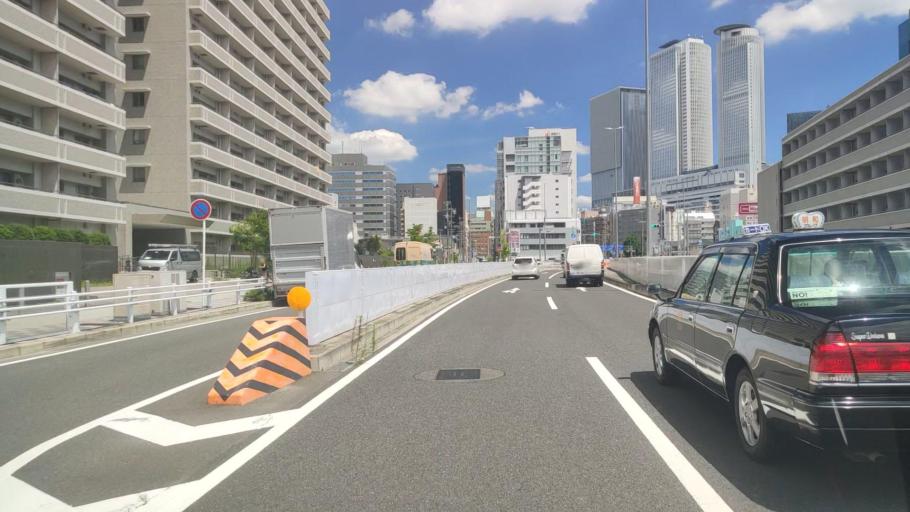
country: JP
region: Aichi
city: Nagoya-shi
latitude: 35.1645
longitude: 136.8803
